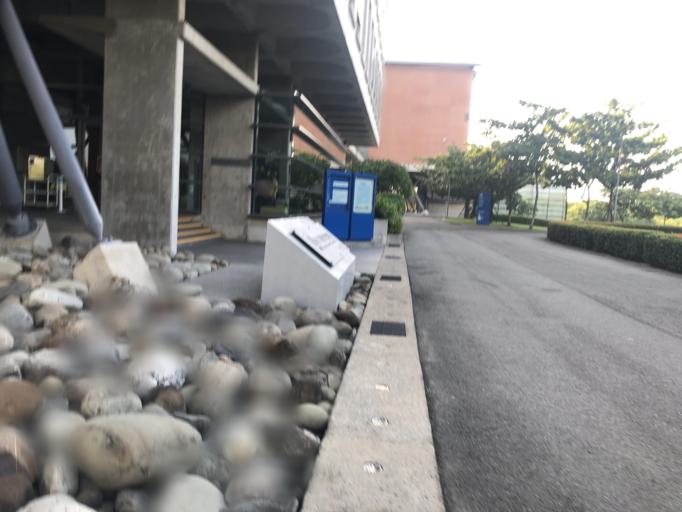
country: TW
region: Taiwan
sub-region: Tainan
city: Tainan
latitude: 23.0584
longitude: 120.2361
